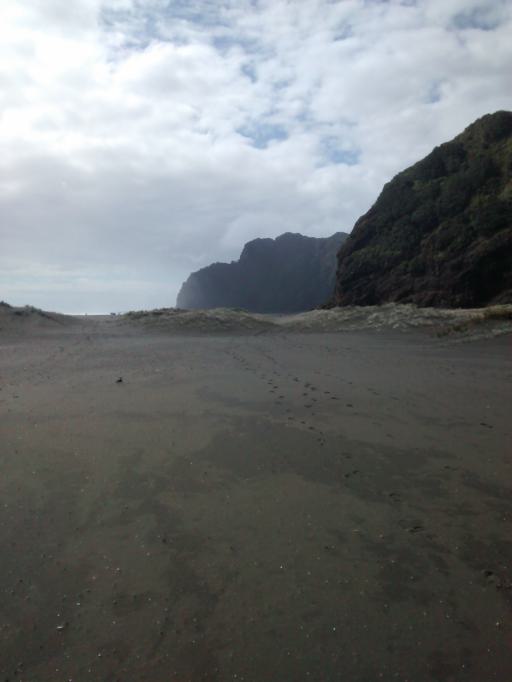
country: NZ
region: Auckland
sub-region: Auckland
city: Muriwai Beach
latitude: -36.9960
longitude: 174.4742
